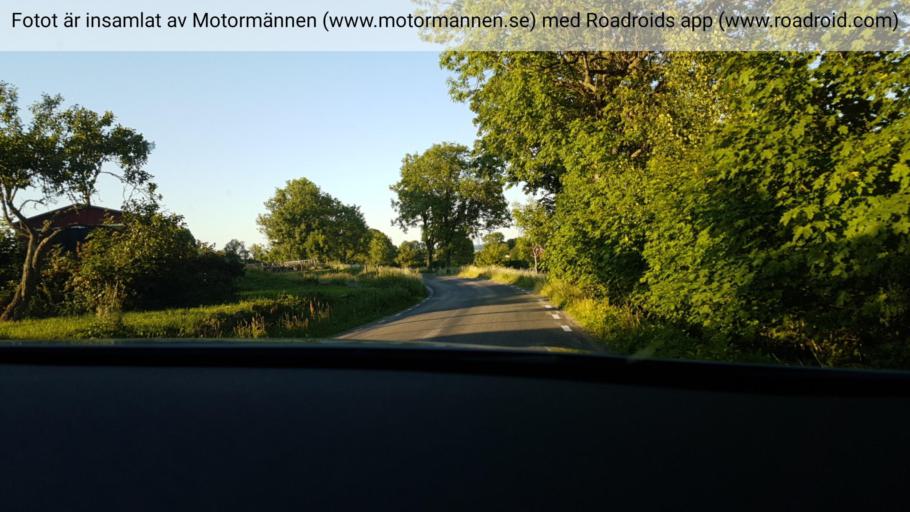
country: SE
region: Vaestra Goetaland
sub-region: Skovde Kommun
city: Skultorp
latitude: 58.2951
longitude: 13.8005
